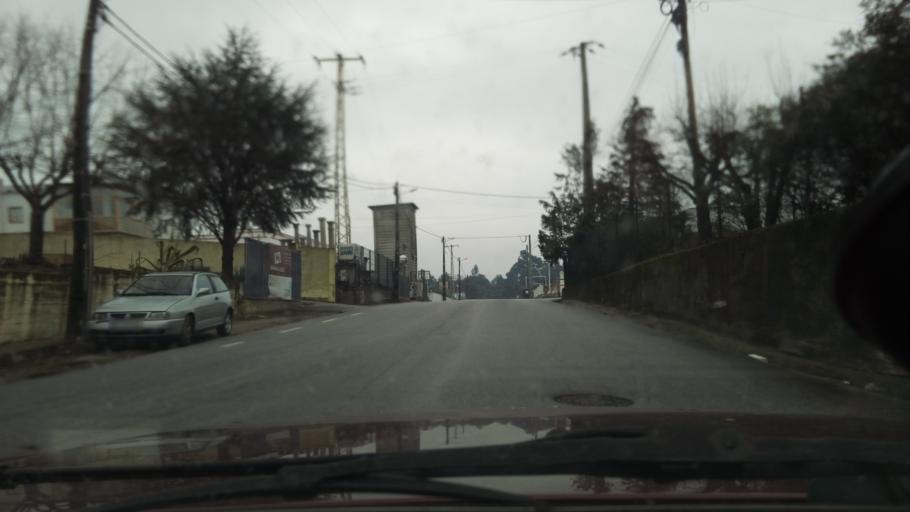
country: PT
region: Viseu
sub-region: Mangualde
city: Mangualde
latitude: 40.6019
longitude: -7.7930
